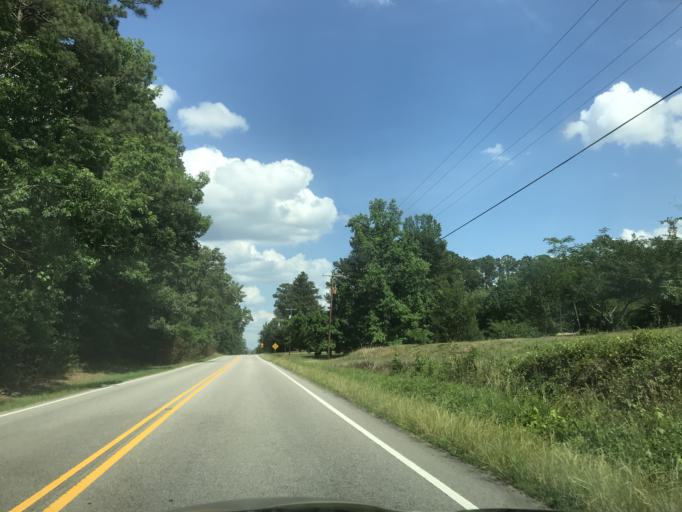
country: US
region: North Carolina
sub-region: Franklin County
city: Louisburg
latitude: 35.9662
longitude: -78.3213
